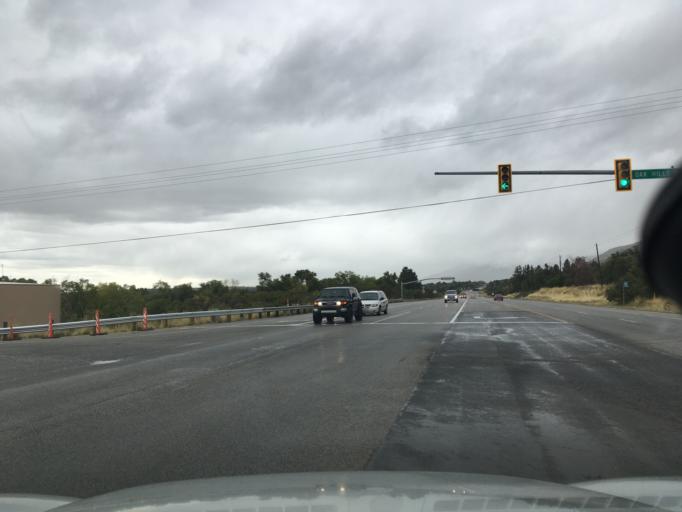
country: US
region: Utah
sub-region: Davis County
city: Fruit Heights
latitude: 41.0661
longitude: -111.9107
